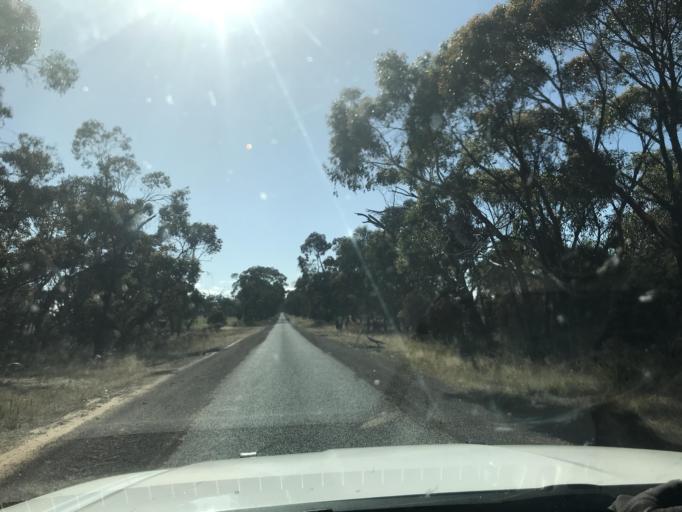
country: AU
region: Victoria
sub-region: Horsham
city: Horsham
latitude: -37.0241
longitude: 141.6944
